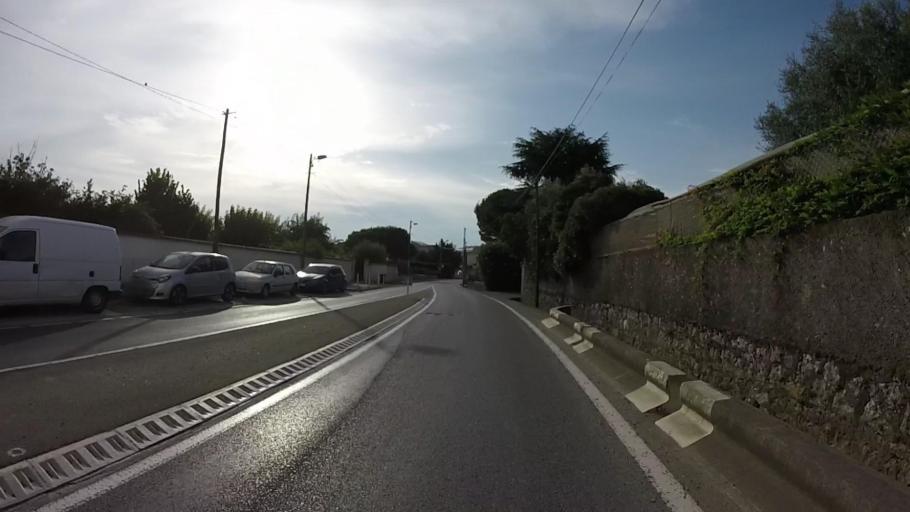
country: FR
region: Provence-Alpes-Cote d'Azur
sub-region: Departement des Alpes-Maritimes
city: Biot
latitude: 43.5964
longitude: 7.1108
